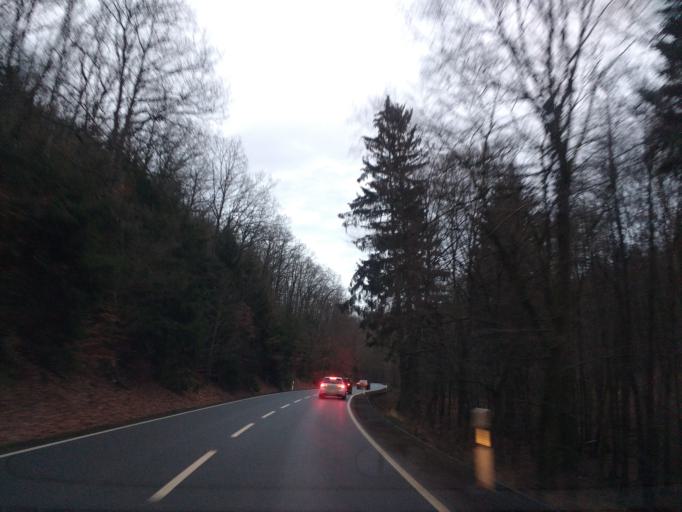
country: DE
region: Saxony-Anhalt
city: Bad Suderode
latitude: 51.7142
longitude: 11.0936
